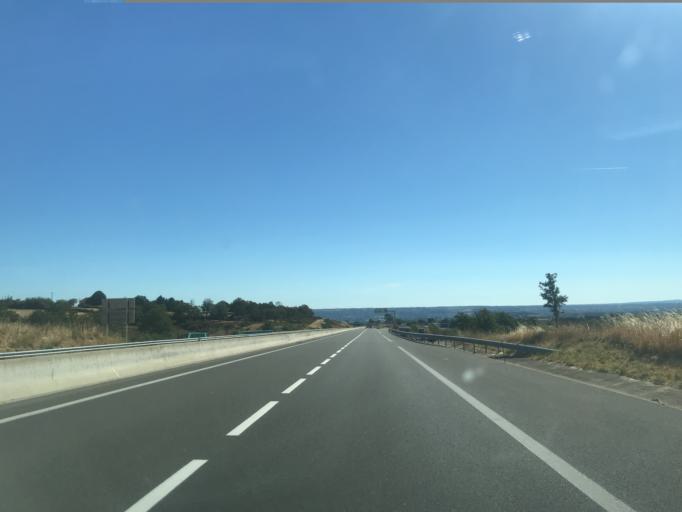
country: FR
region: Auvergne
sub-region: Departement de l'Allier
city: Quinssaines
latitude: 46.3193
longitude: 2.5105
